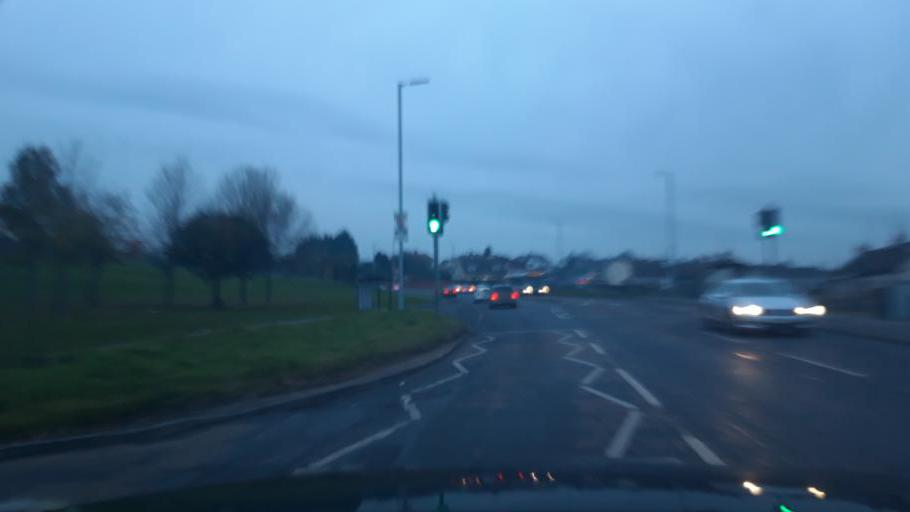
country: GB
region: Northern Ireland
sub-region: Newry and Mourne District
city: Newry
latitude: 54.1840
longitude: -6.3560
